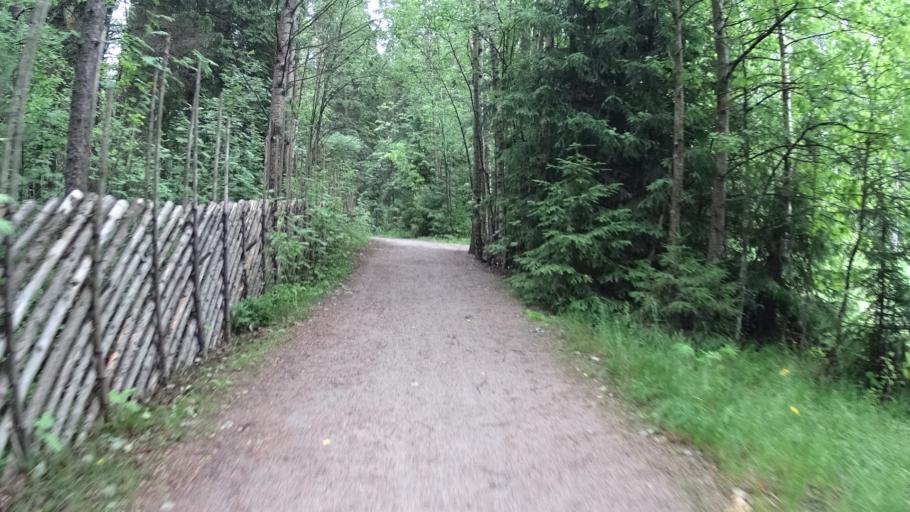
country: FI
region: Uusimaa
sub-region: Helsinki
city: Teekkarikylae
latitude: 60.2684
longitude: 24.9011
